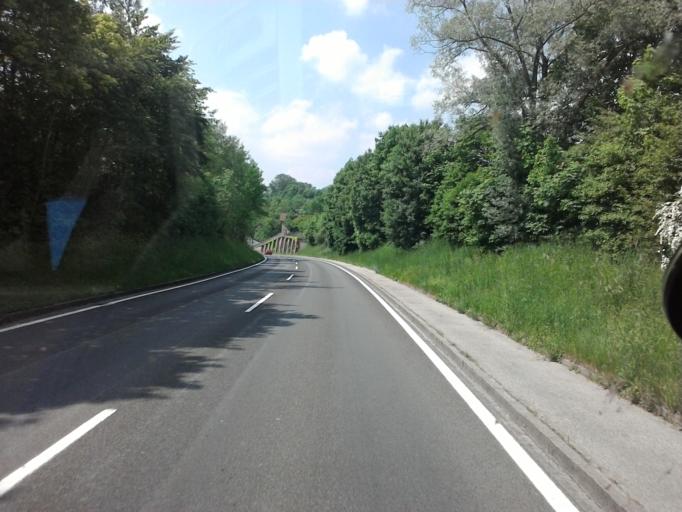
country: AT
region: Upper Austria
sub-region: Politischer Bezirk Steyr-Land
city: Garsten
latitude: 48.0449
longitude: 14.3785
